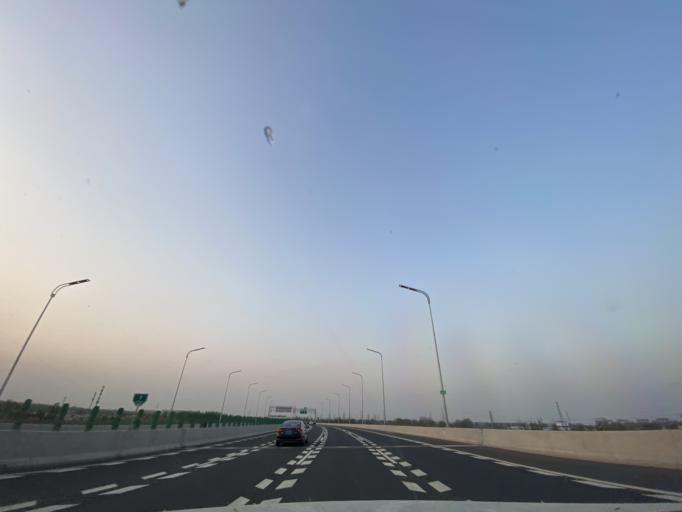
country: CN
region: Beijing
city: Xingfeng
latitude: 39.6985
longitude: 116.3784
